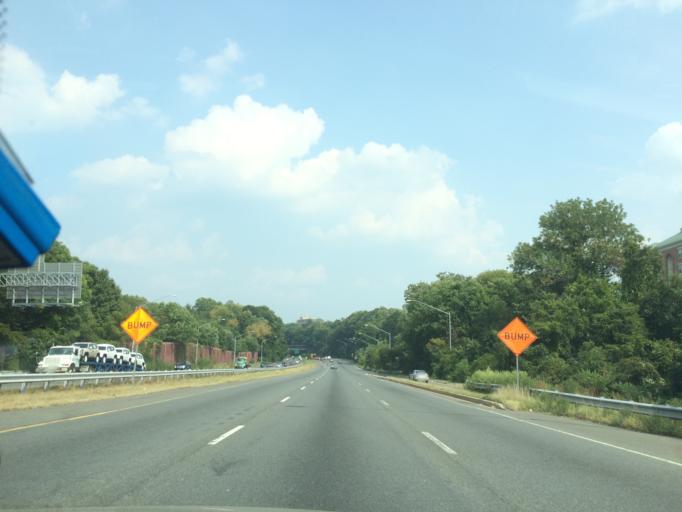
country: US
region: Maryland
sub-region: Montgomery County
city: North Bethesda
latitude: 39.0157
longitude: -77.1178
